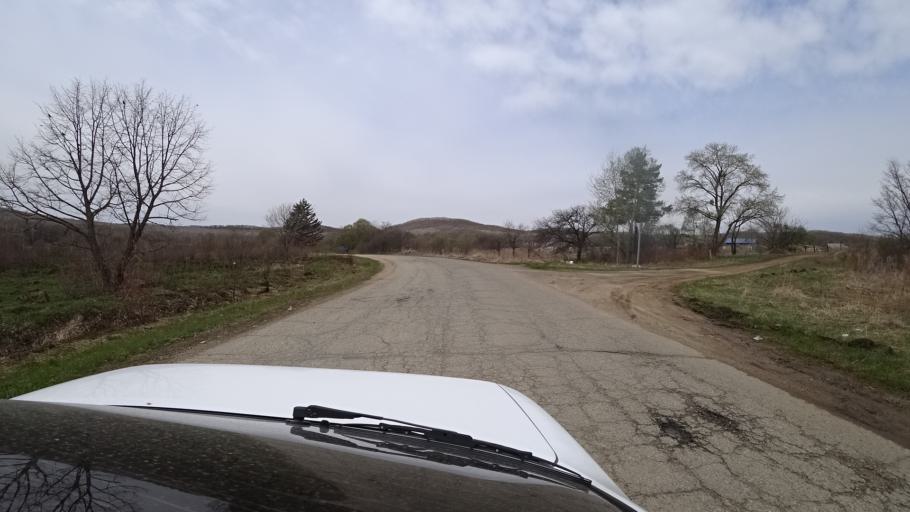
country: RU
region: Primorskiy
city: Dal'nerechensk
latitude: 45.7994
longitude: 134.1005
